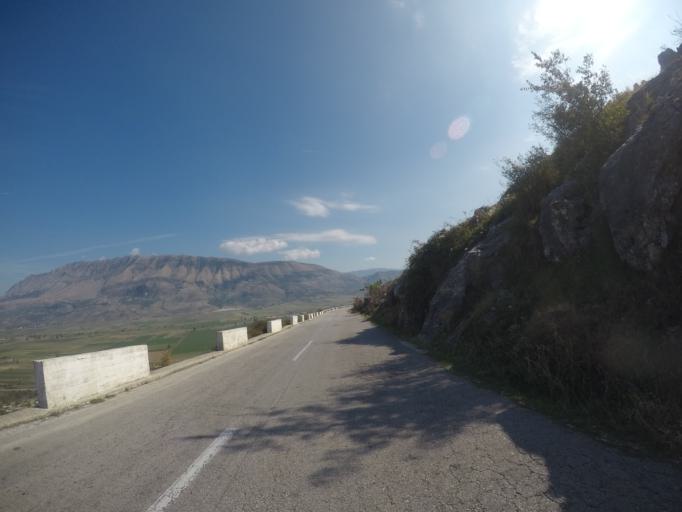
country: AL
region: Gjirokaster
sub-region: Rrethi i Gjirokastres
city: Libohove
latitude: 39.9483
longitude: 20.2459
